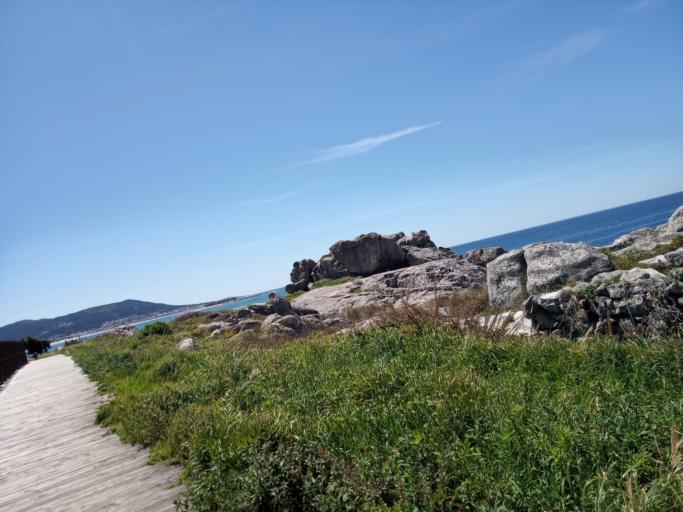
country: ES
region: Galicia
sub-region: Provincia de Pontevedra
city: A Guarda
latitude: 41.8740
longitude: -8.8752
